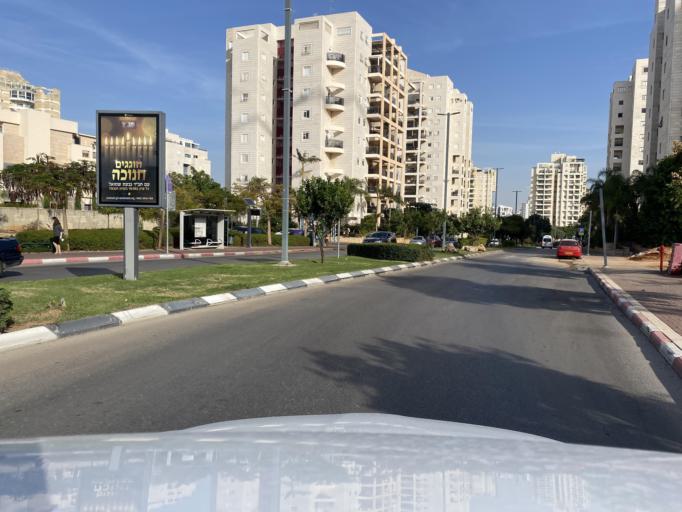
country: IL
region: Tel Aviv
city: Giv`at Shemu'el
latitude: 32.0730
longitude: 34.8515
